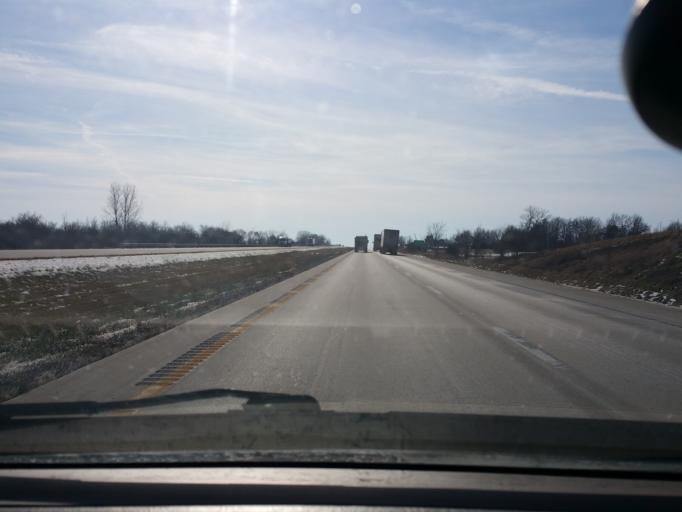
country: US
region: Missouri
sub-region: Clinton County
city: Cameron
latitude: 39.6555
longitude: -94.2389
